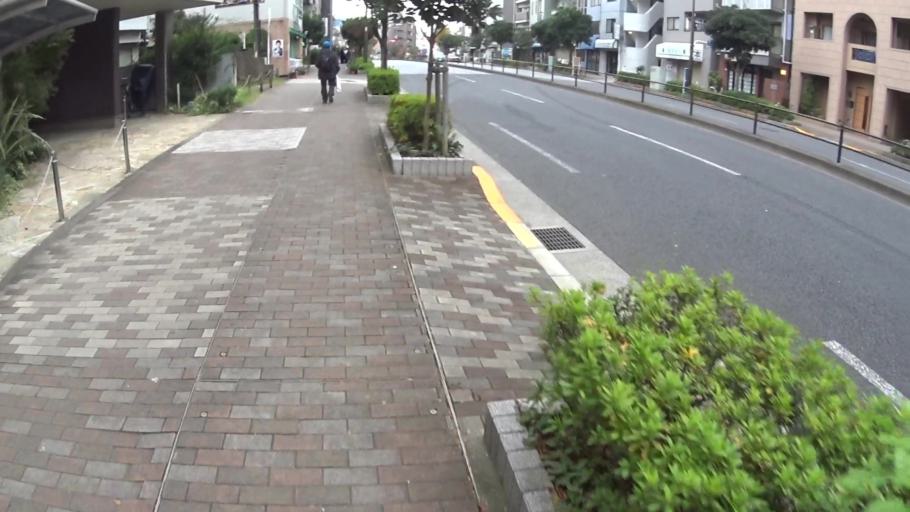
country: JP
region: Tokyo
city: Tokyo
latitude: 35.6957
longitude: 139.7163
